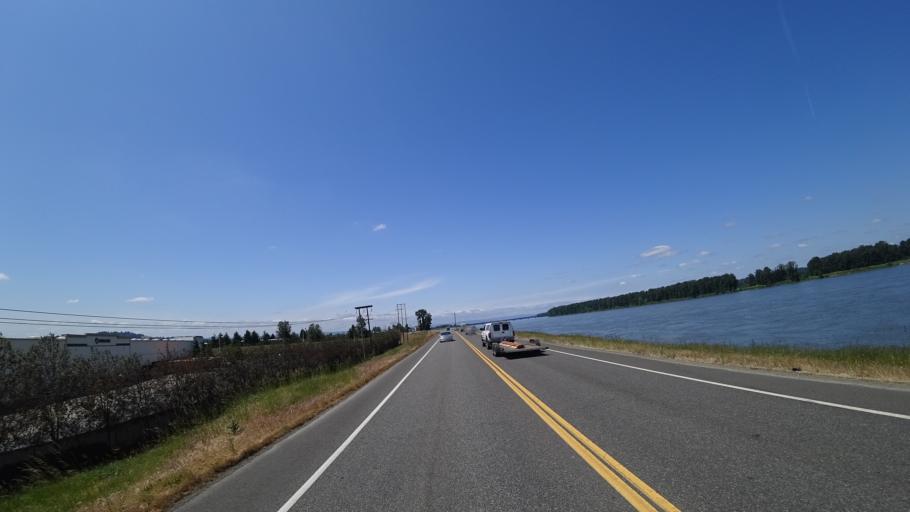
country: US
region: Washington
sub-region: Clark County
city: Mill Plain
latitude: 45.5639
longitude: -122.5131
